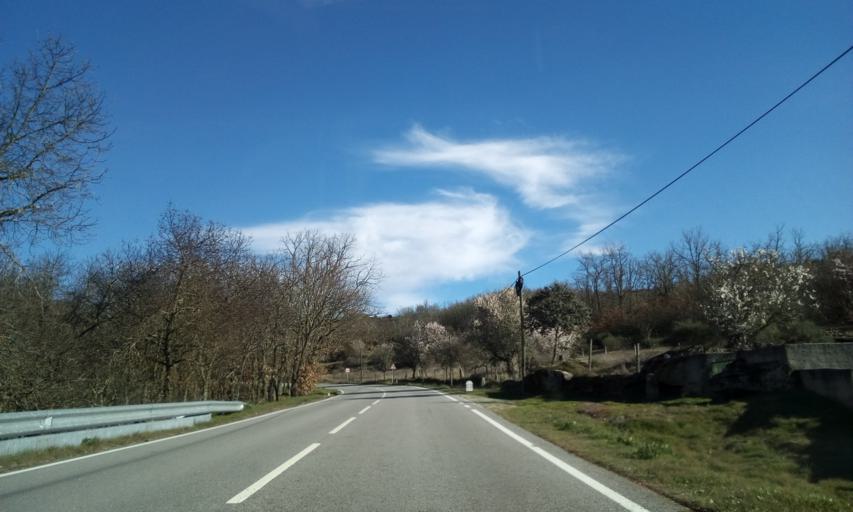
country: ES
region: Castille and Leon
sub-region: Provincia de Salamanca
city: Fuentes de Onoro
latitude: 40.6170
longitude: -6.9051
